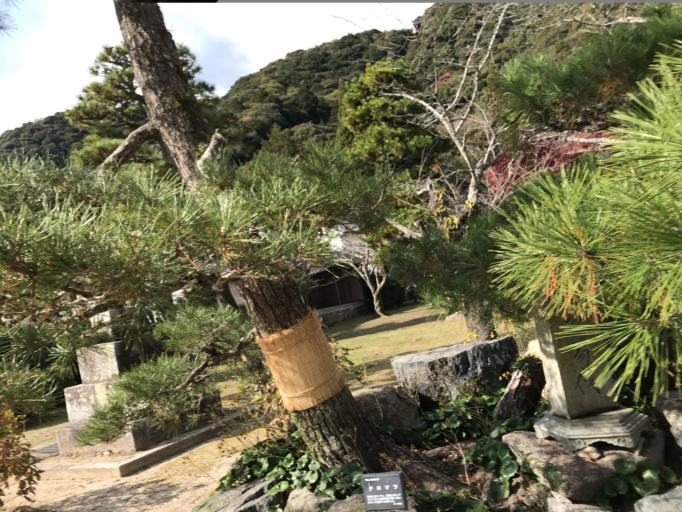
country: JP
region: Yamaguchi
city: Iwakuni
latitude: 34.1716
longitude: 132.1762
